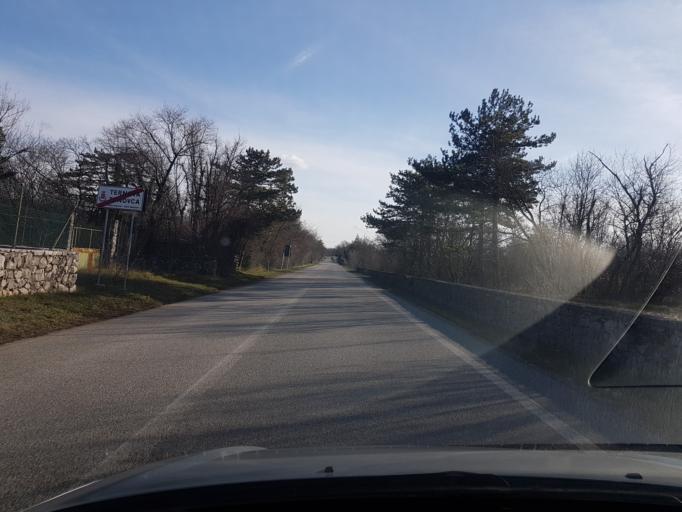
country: IT
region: Friuli Venezia Giulia
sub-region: Provincia di Trieste
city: Santa Croce
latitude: 45.7595
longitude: 13.7064
